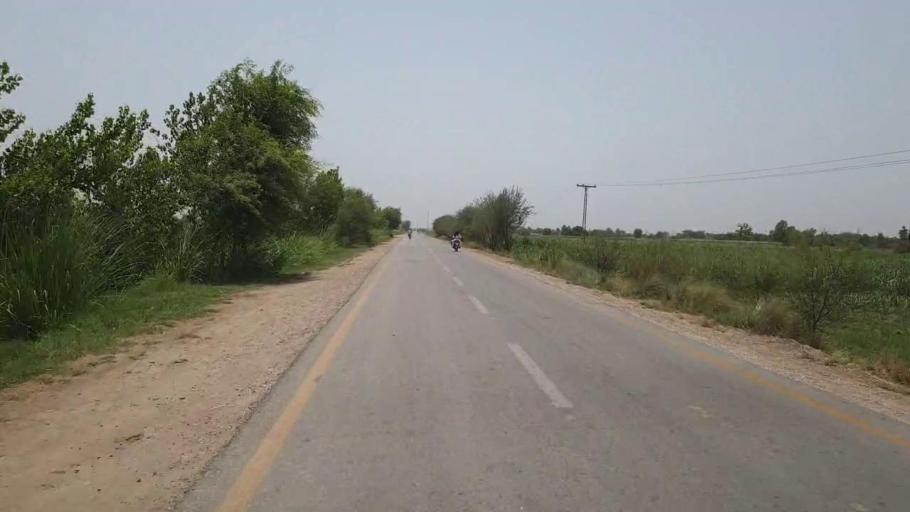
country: PK
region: Sindh
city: Moro
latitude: 26.6002
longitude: 68.0858
